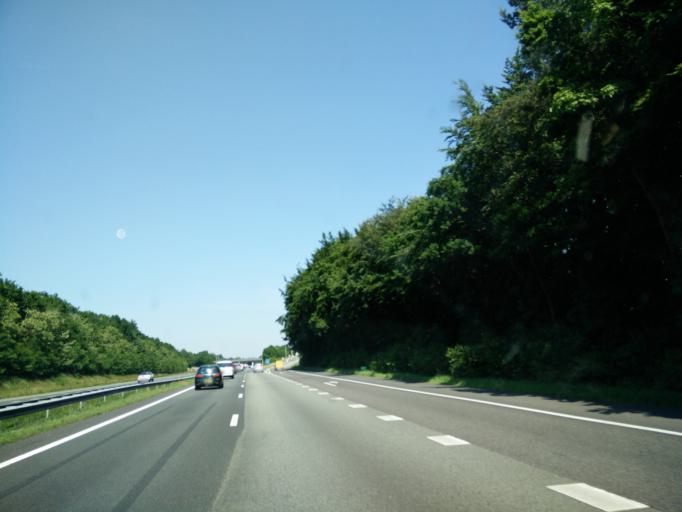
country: NL
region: Gelderland
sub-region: Gemeente Harderwijk
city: Harderwijk
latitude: 52.3344
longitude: 5.6394
